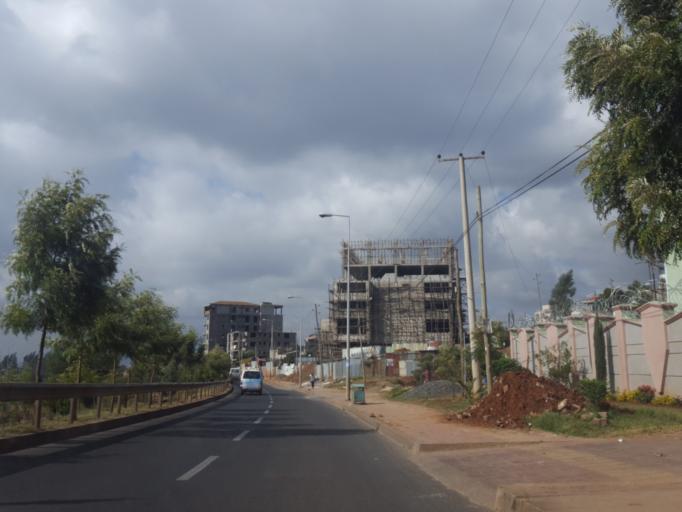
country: ET
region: Adis Abeba
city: Addis Ababa
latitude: 9.0695
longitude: 38.7176
